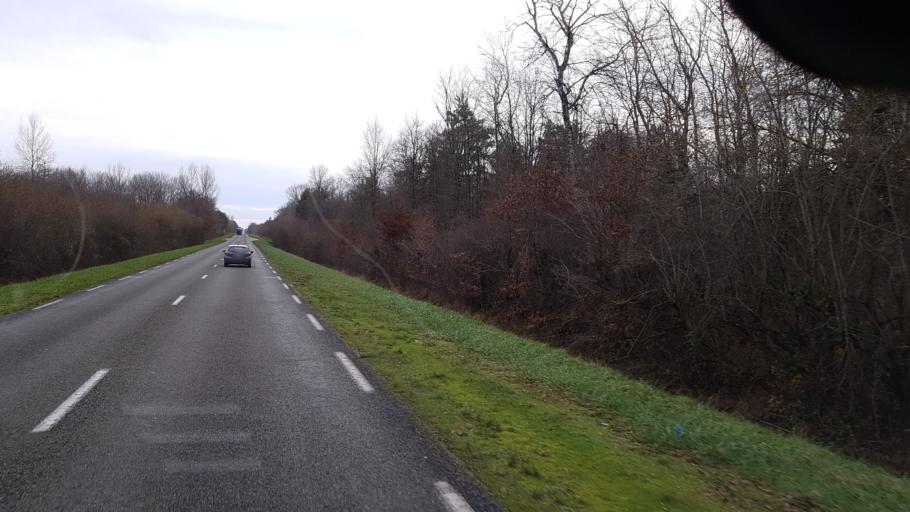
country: FR
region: Centre
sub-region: Departement du Loiret
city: La Ferte-Saint-Aubin
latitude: 47.6954
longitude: 1.9530
